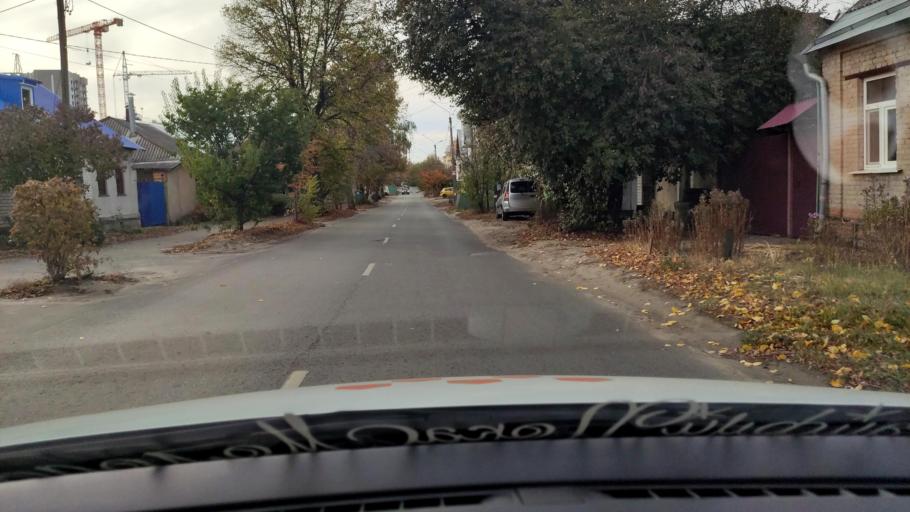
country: RU
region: Voronezj
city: Voronezh
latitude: 51.6657
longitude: 39.1707
